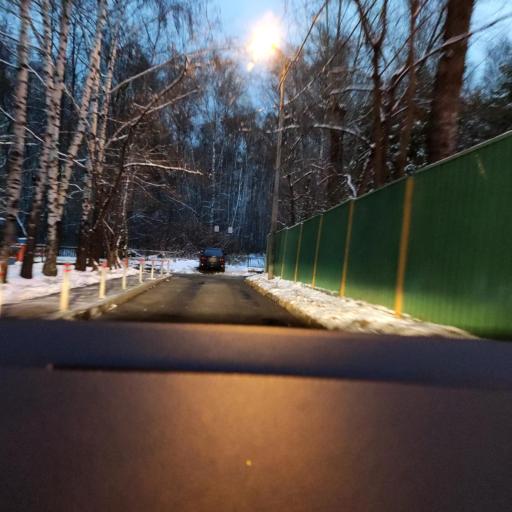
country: RU
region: Moscow
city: Metrogorodok
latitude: 55.8219
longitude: 37.7906
